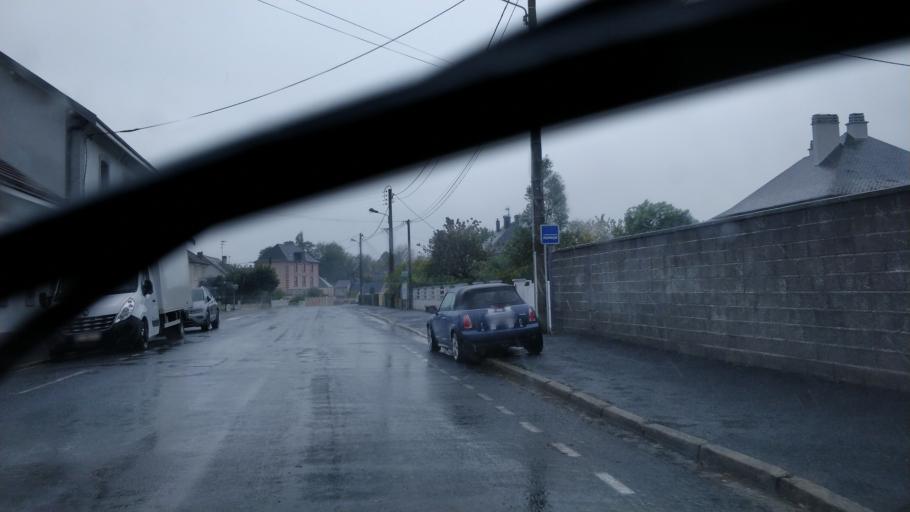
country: FR
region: Lower Normandy
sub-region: Departement de la Manche
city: Brehal
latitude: 48.8979
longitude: -1.5115
